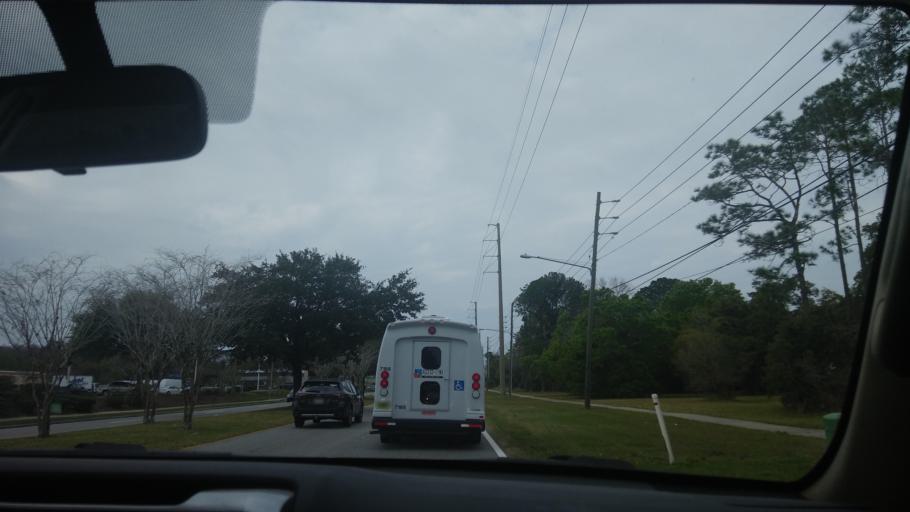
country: US
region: Florida
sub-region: Orange County
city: Williamsburg
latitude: 28.4083
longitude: -81.4485
